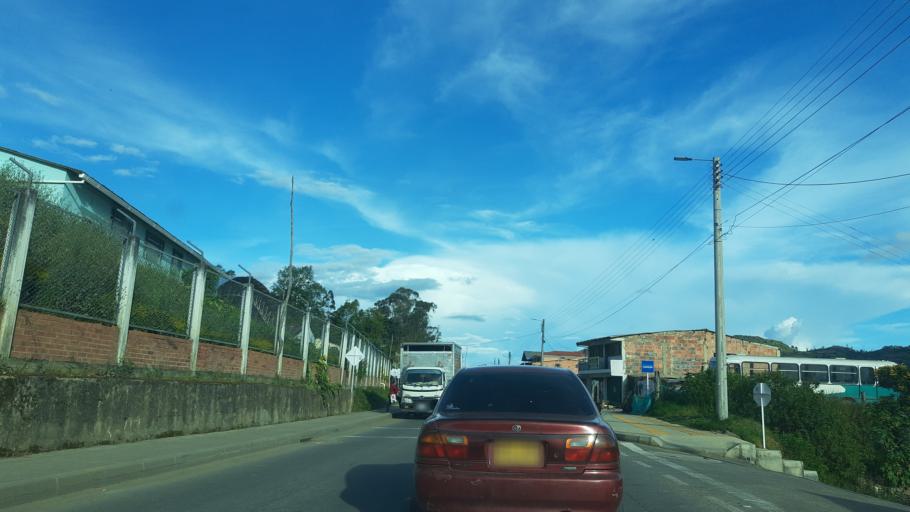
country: CO
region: Cundinamarca
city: Macheta
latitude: 5.0787
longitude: -73.6080
